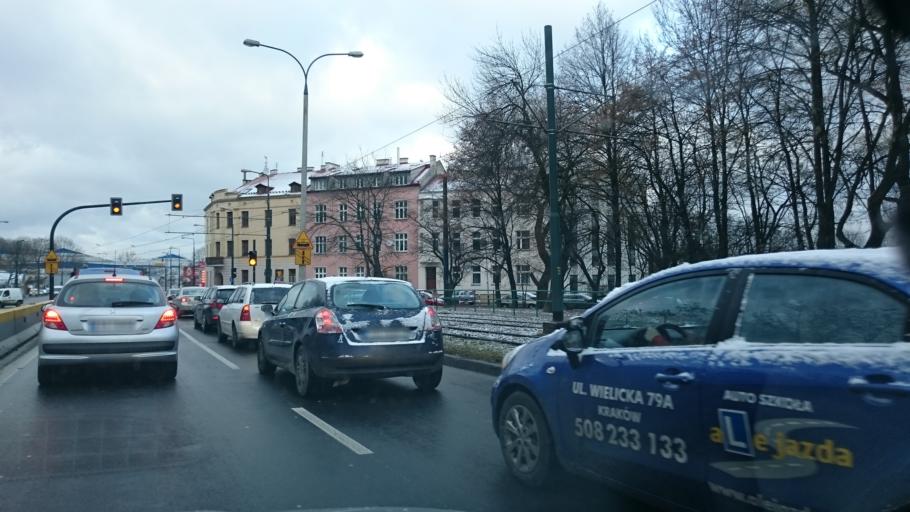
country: PL
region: Lesser Poland Voivodeship
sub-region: Krakow
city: Krakow
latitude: 50.0392
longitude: 19.9642
